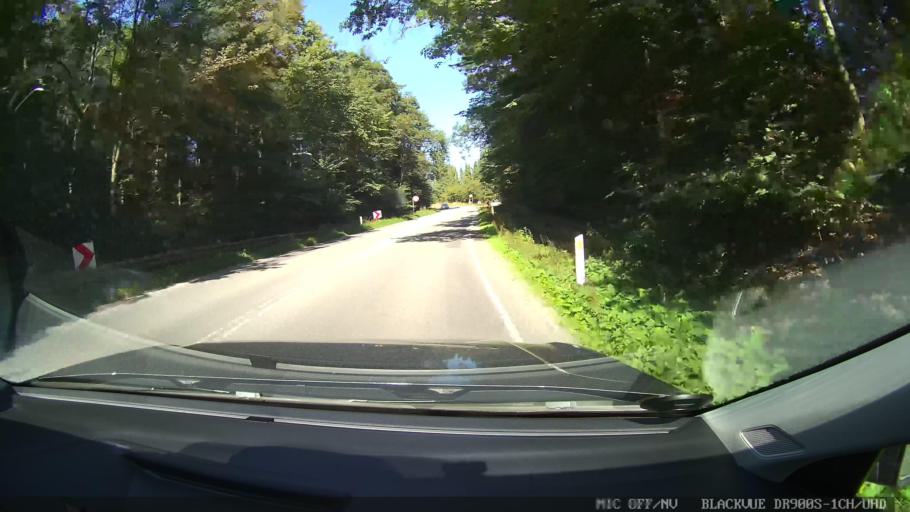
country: DK
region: North Denmark
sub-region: Mariagerfjord Kommune
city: Mariager
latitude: 56.6078
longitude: 9.9953
